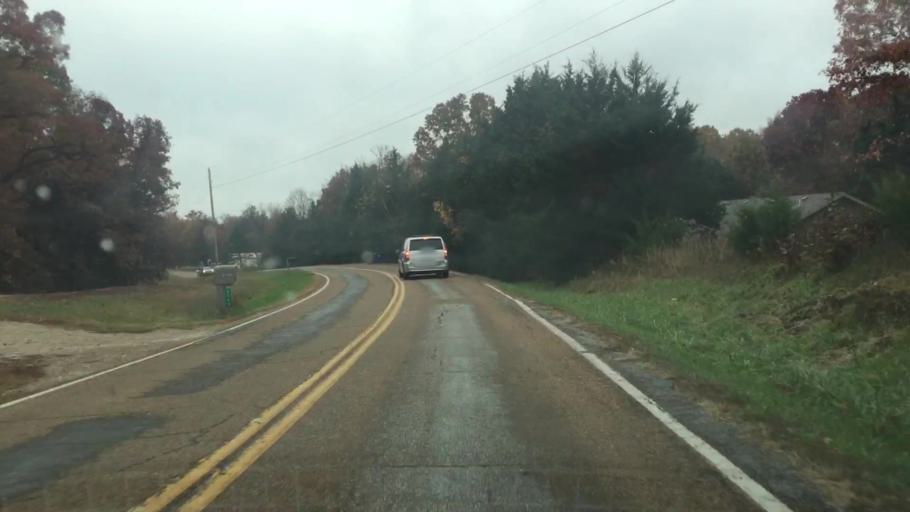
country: US
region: Missouri
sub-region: Callaway County
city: Fulton
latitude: 38.7374
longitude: -91.7060
